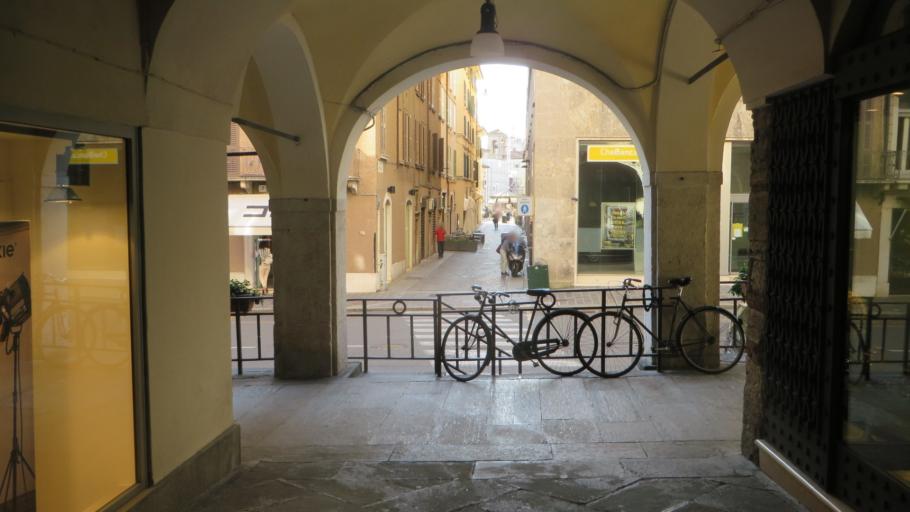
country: IT
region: Lombardy
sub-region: Provincia di Brescia
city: Brescia
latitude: 45.5374
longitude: 10.2202
